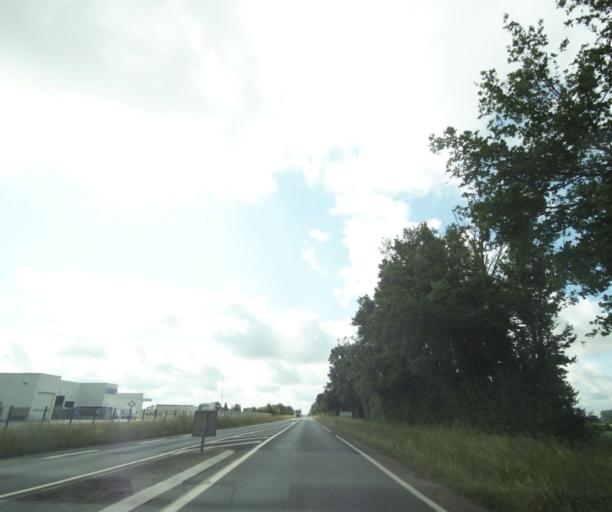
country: FR
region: Pays de la Loire
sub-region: Departement de la Sarthe
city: Solesmes
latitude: 47.8205
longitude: -0.2972
